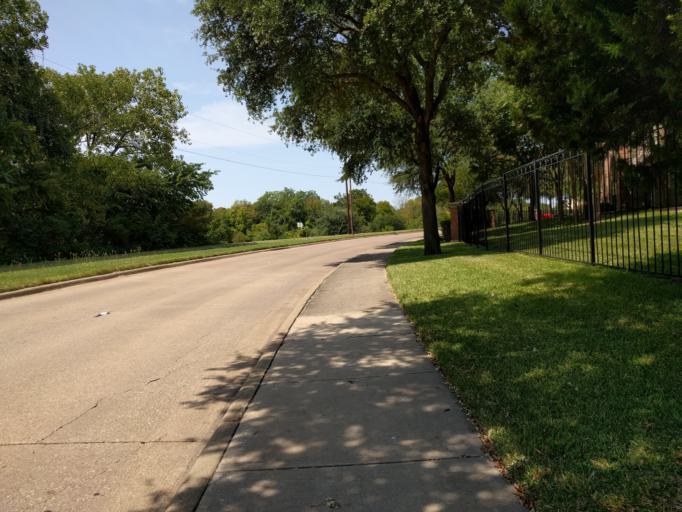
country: US
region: Texas
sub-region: Dallas County
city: Richardson
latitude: 32.9183
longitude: -96.7766
